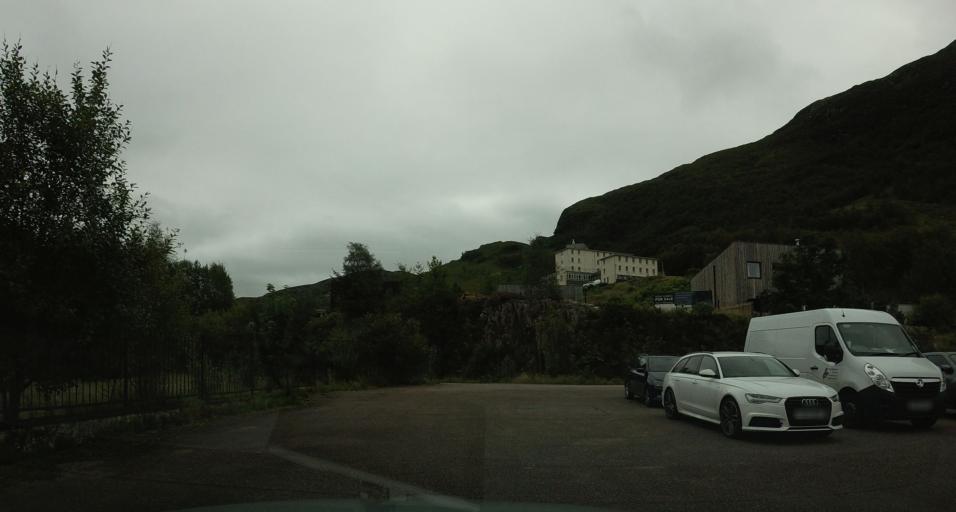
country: GB
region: Scotland
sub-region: Highland
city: Fort William
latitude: 56.7130
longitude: -4.9624
